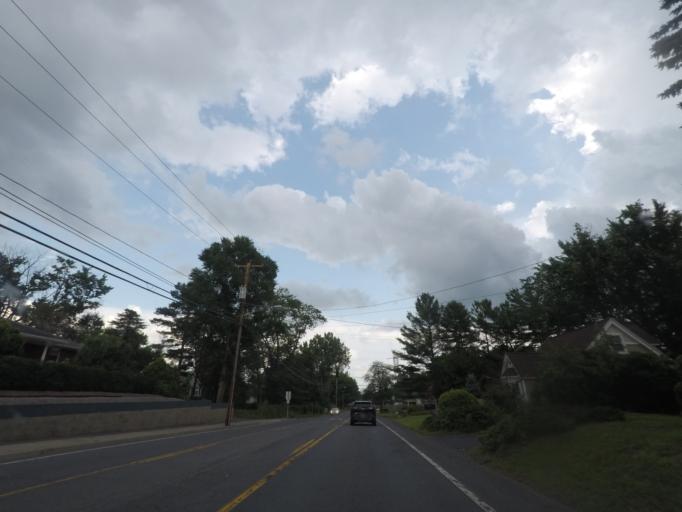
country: US
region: New York
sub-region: Albany County
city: Roessleville
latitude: 42.6998
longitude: -73.7943
